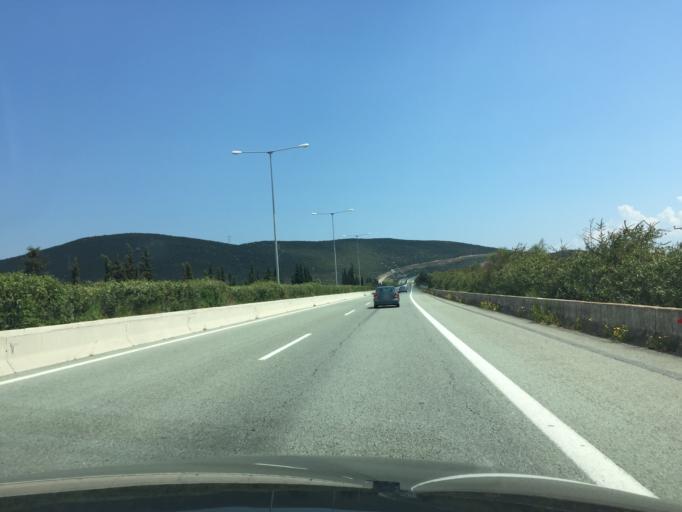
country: GR
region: Central Greece
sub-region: Nomos Fthiotidos
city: Pelasgia
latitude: 38.8906
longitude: 22.8091
